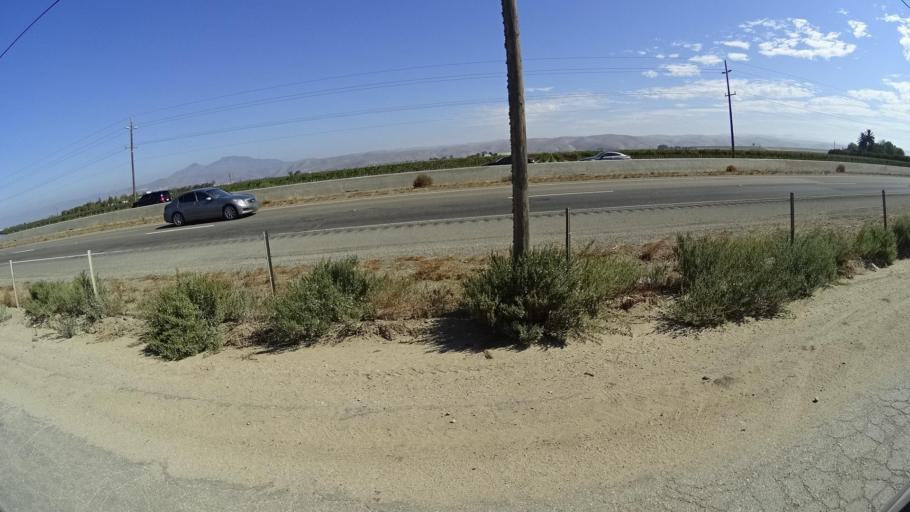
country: US
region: California
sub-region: Monterey County
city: Greenfield
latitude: 36.3032
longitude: -121.2235
